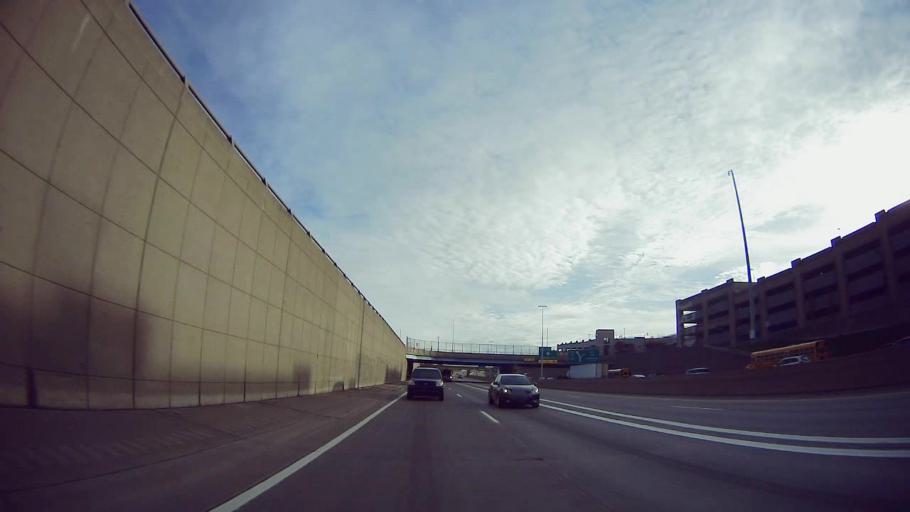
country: US
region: Michigan
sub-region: Wayne County
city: Detroit
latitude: 42.3406
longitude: -83.0516
